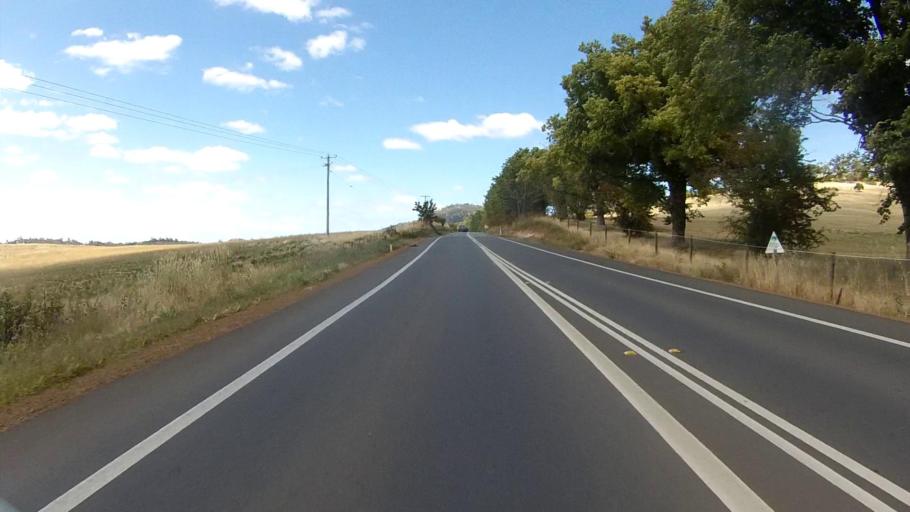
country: AU
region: Tasmania
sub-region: Clarence
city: Cambridge
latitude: -42.8043
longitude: 147.4230
